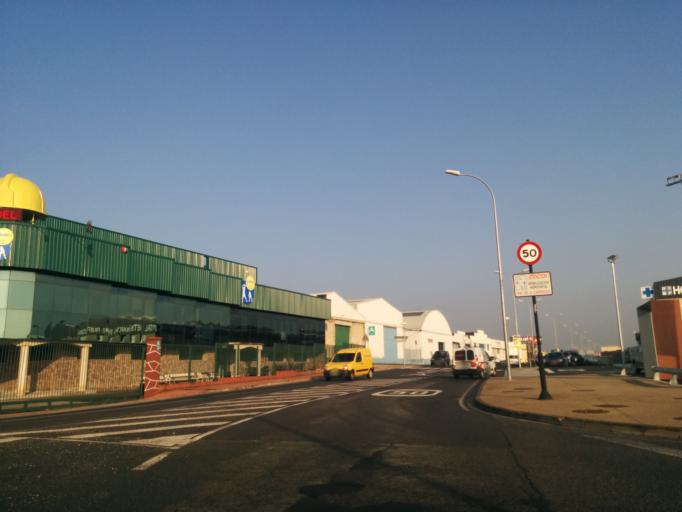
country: ES
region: Navarre
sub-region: Provincia de Navarra
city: Segundo Ensanche
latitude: 42.7840
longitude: -1.6230
